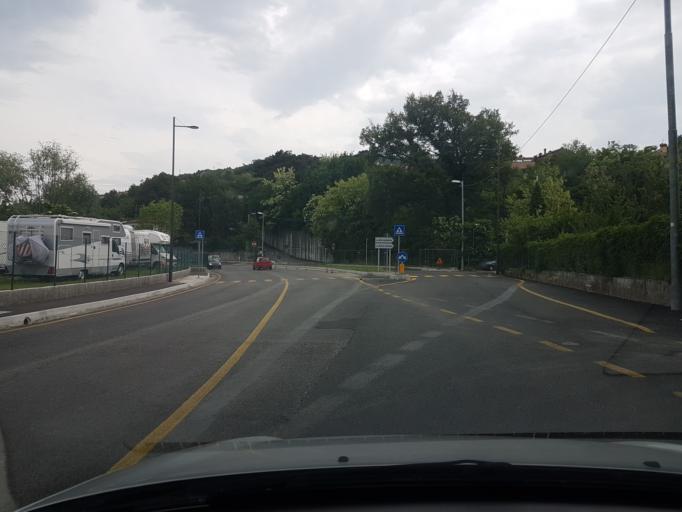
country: IT
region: Friuli Venezia Giulia
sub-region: Provincia di Trieste
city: Muggia
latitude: 45.5969
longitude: 13.7851
